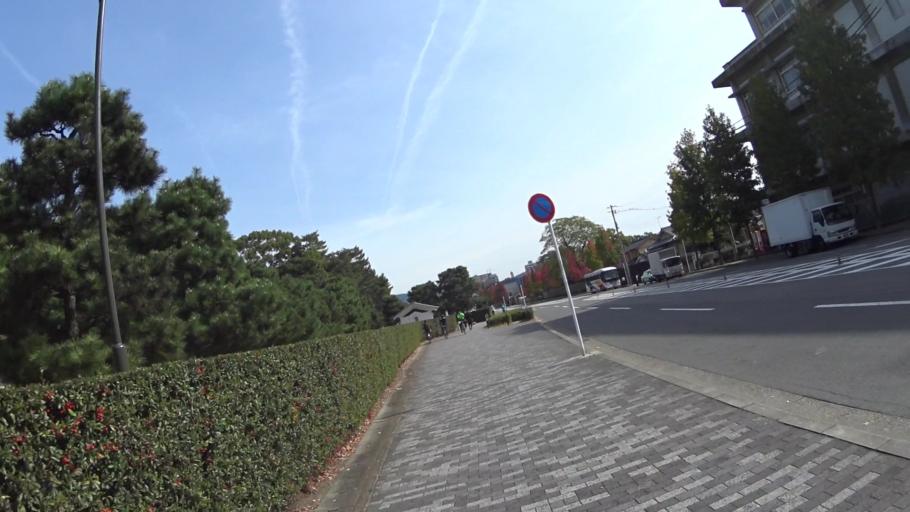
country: JP
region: Kyoto
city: Kyoto
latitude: 35.0122
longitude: 135.7467
